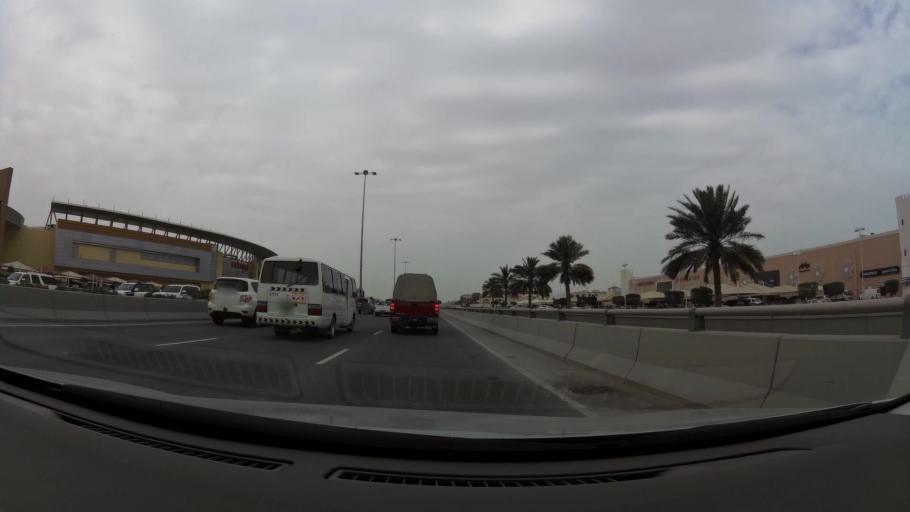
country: QA
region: Baladiyat ar Rayyan
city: Ar Rayyan
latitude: 25.3325
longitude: 51.4642
